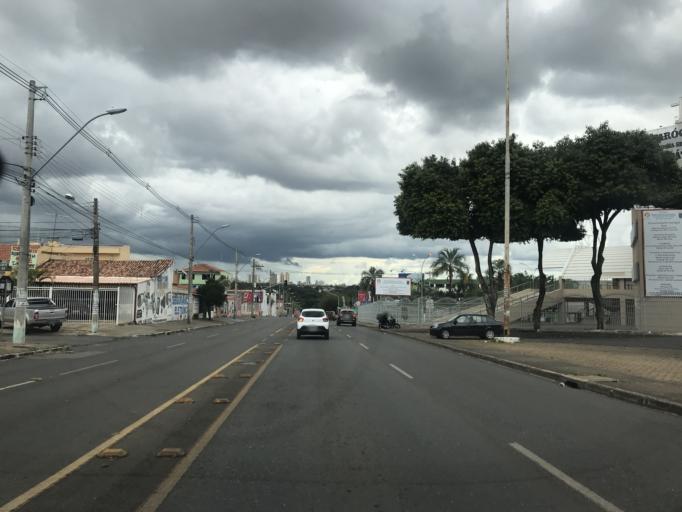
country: BR
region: Federal District
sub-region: Brasilia
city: Brasilia
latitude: -15.8436
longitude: -48.0493
